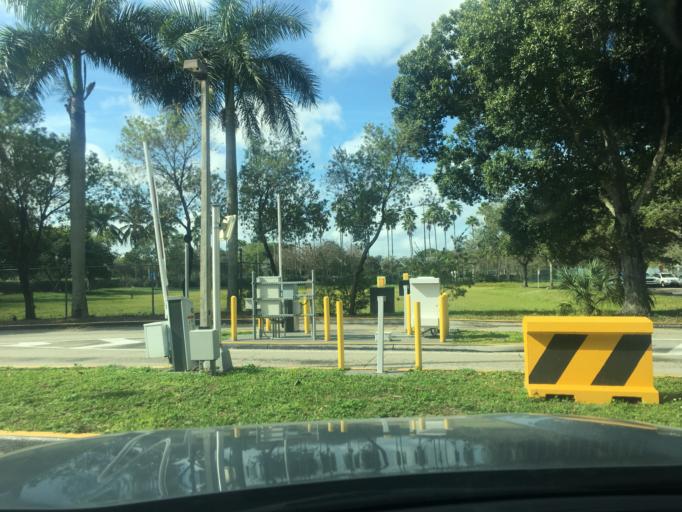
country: US
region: Florida
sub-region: Broward County
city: Dania Beach
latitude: 26.0705
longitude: -80.1727
